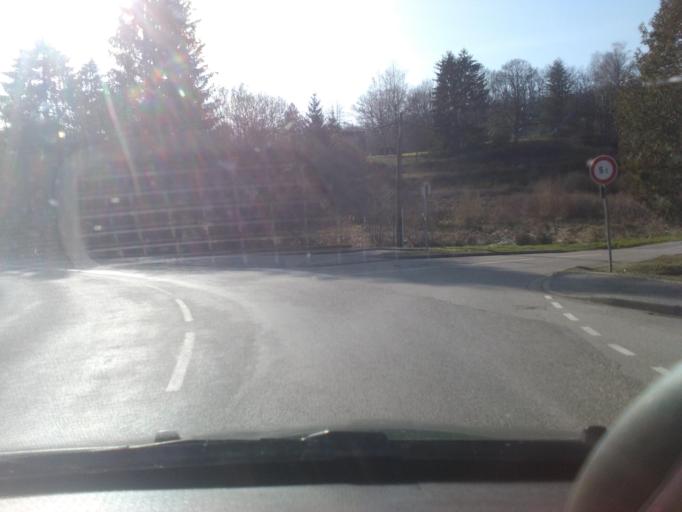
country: FR
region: Lorraine
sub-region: Departement des Vosges
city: Sainte-Marguerite
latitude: 48.2860
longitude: 6.9877
